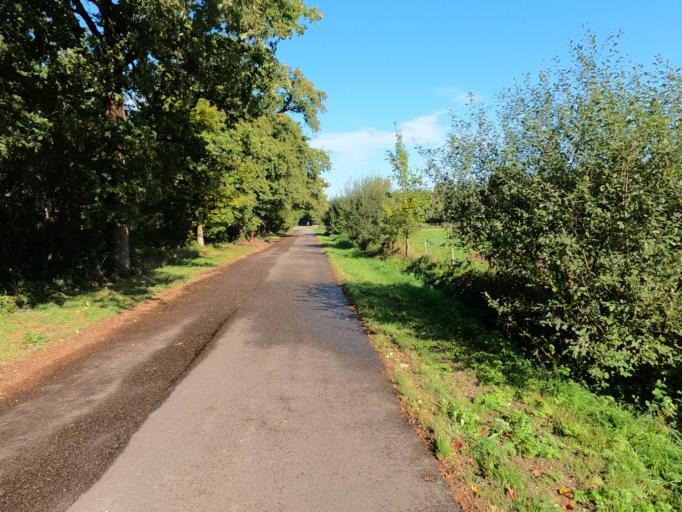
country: BE
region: Flanders
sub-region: Provincie Antwerpen
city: Zandhoven
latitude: 51.2324
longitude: 4.6603
